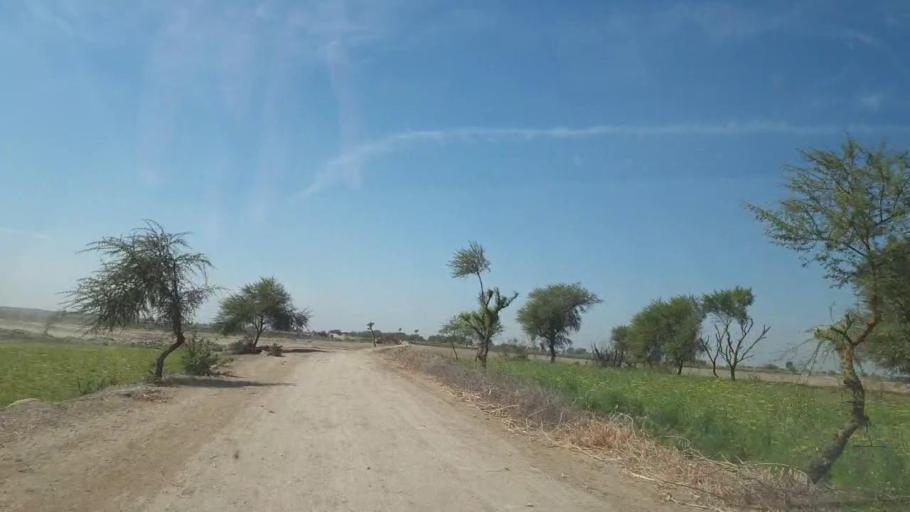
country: PK
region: Sindh
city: Pithoro
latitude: 25.6243
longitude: 69.2454
